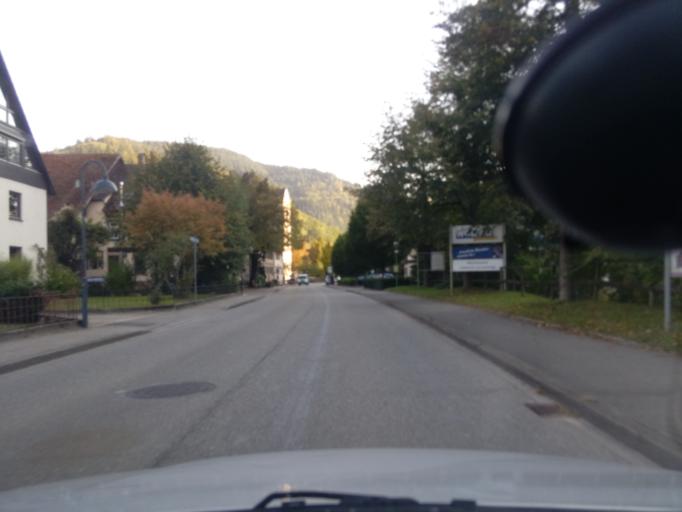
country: DE
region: Baden-Wuerttemberg
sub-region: Freiburg Region
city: Wolfach
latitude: 48.3029
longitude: 8.2208
